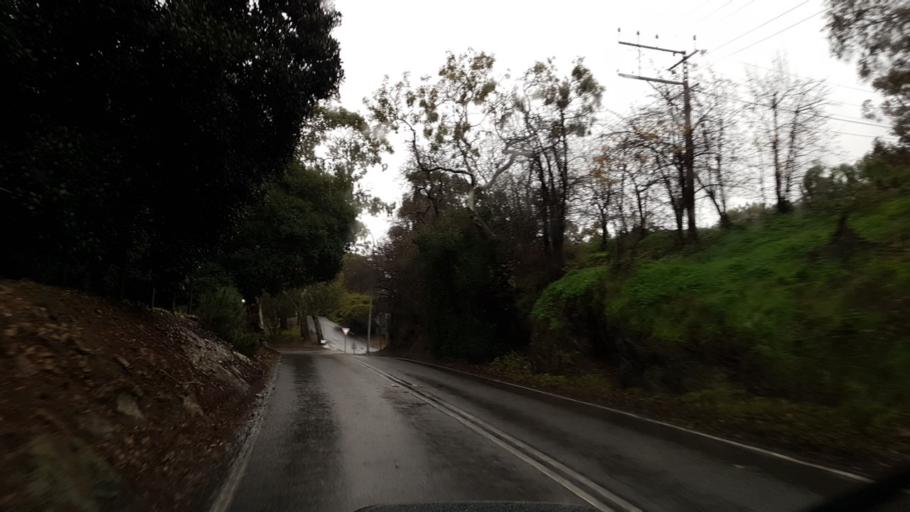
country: AU
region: South Australia
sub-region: Onkaparinga
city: Craigburn Farm
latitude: -35.0526
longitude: 138.6209
